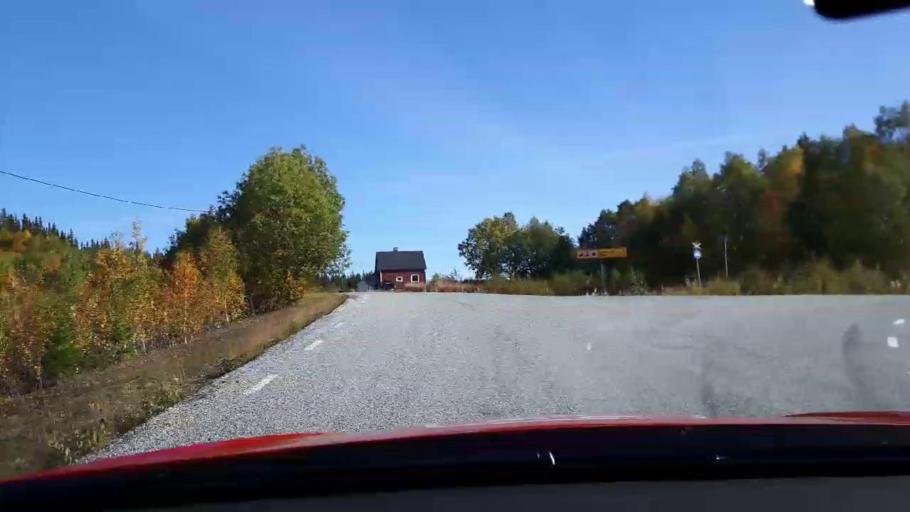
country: NO
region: Nord-Trondelag
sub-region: Royrvik
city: Royrvik
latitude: 64.8748
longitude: 14.2383
